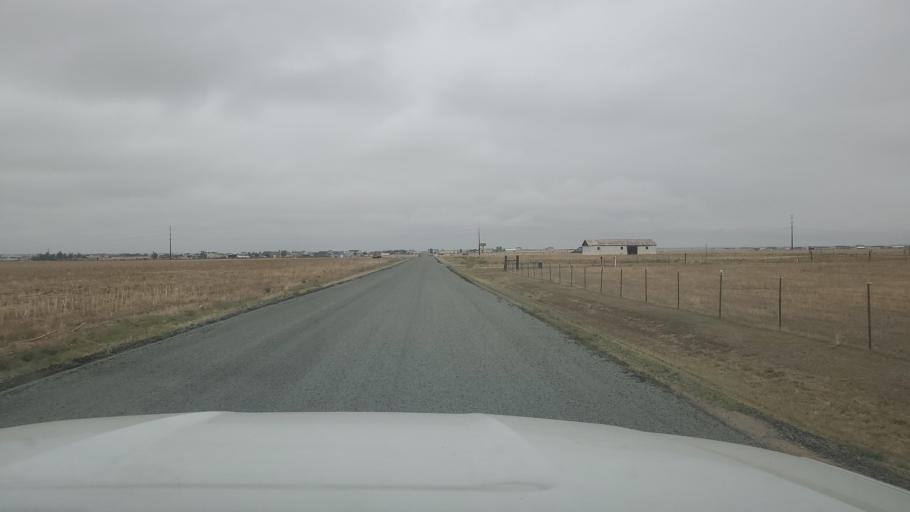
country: US
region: Colorado
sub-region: Weld County
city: Lochbuie
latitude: 39.9367
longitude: -104.6028
